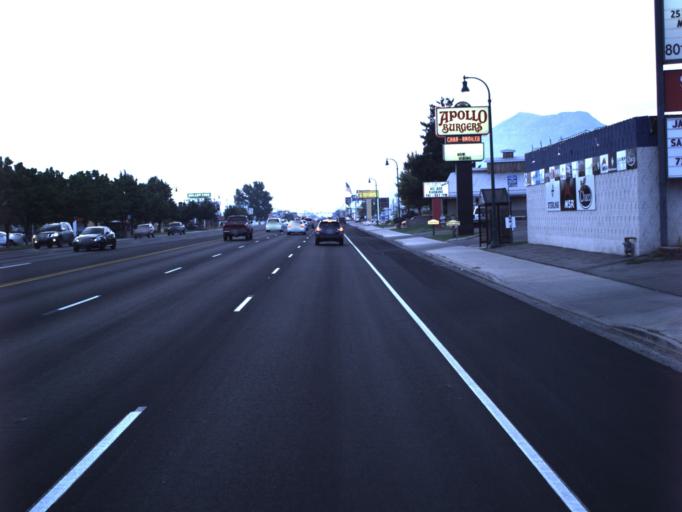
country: US
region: Utah
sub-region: Utah County
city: Orem
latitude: 40.3048
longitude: -111.6982
